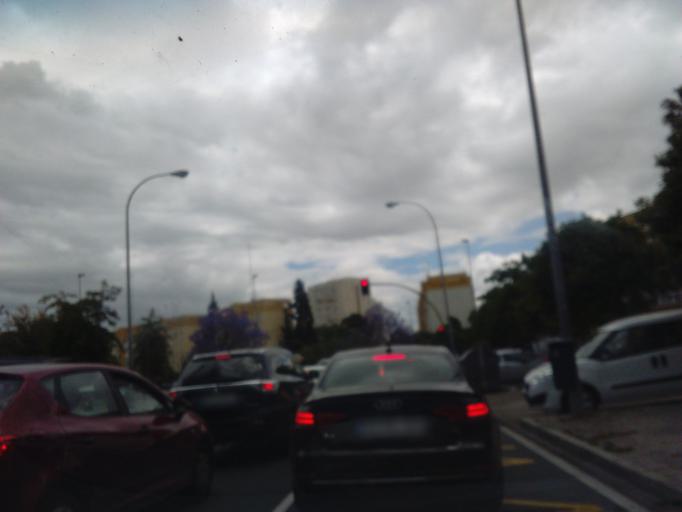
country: ES
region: Andalusia
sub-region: Provincia de Sevilla
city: Sevilla
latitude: 37.3787
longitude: -5.9526
